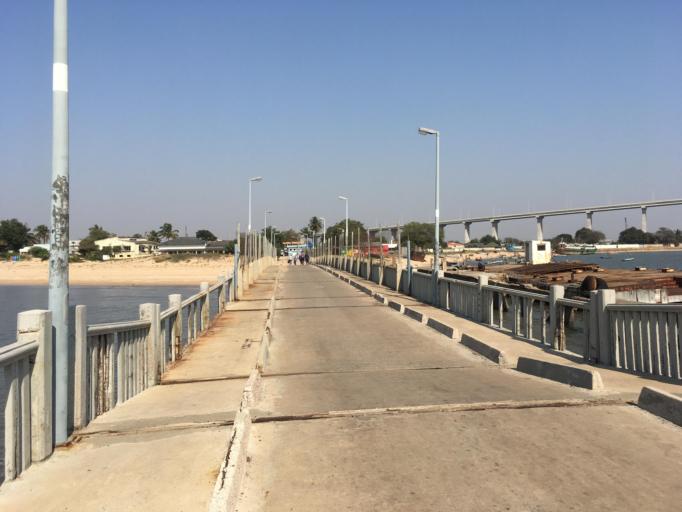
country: MZ
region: Maputo City
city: Maputo
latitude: -25.9796
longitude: 32.5636
